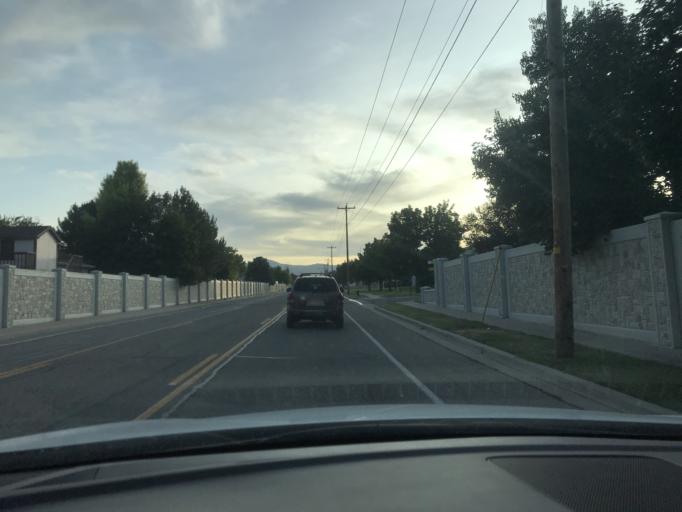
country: US
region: Utah
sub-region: Salt Lake County
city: South Jordan Heights
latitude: 40.5733
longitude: -111.9532
